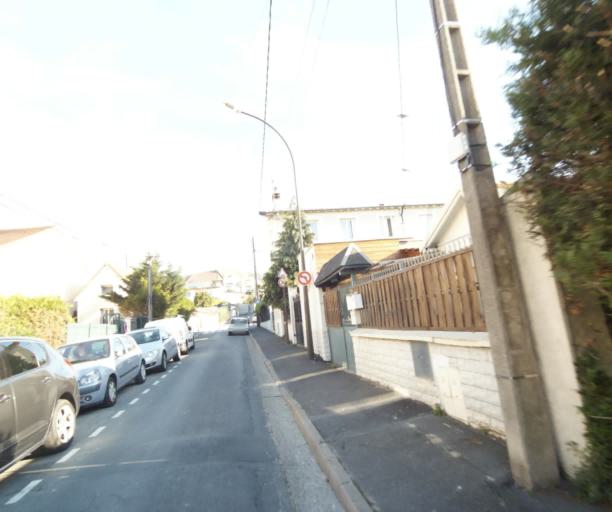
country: FR
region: Ile-de-France
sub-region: Departement du Val-d'Oise
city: Argenteuil
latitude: 48.9386
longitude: 2.2312
